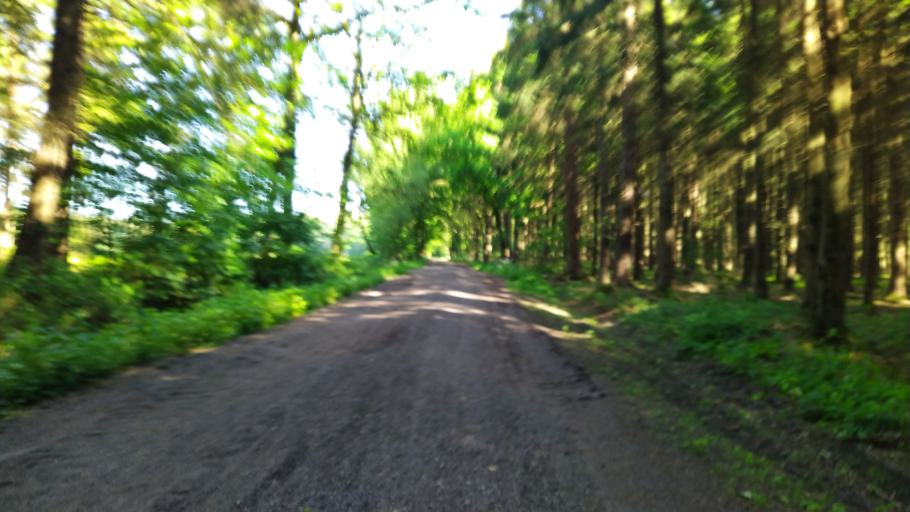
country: DE
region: Lower Saxony
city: Ahlerstedt
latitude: 53.4235
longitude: 9.4777
